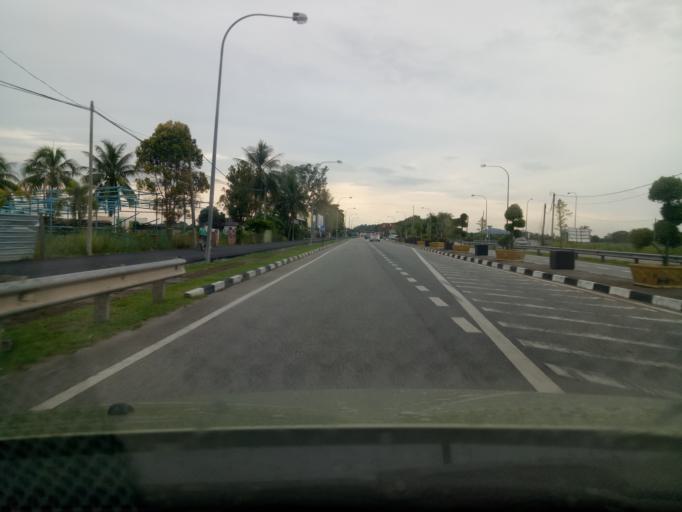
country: MY
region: Kedah
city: Gurun
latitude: 5.9758
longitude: 100.4479
